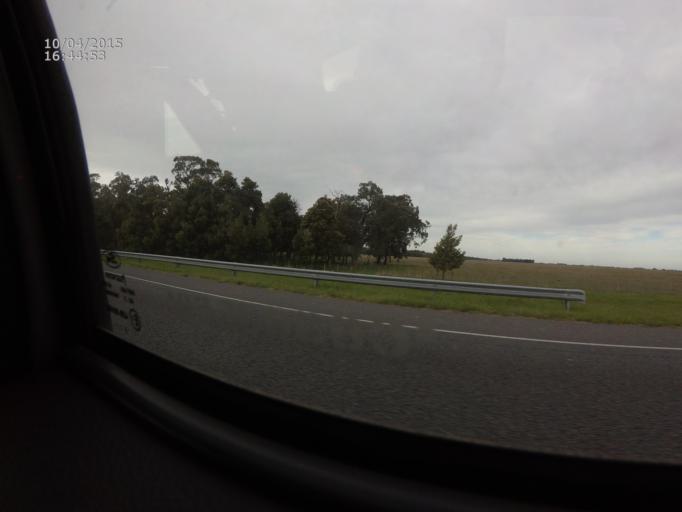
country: AR
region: Buenos Aires
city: Coronel Vidal
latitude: -37.7181
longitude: -57.6532
